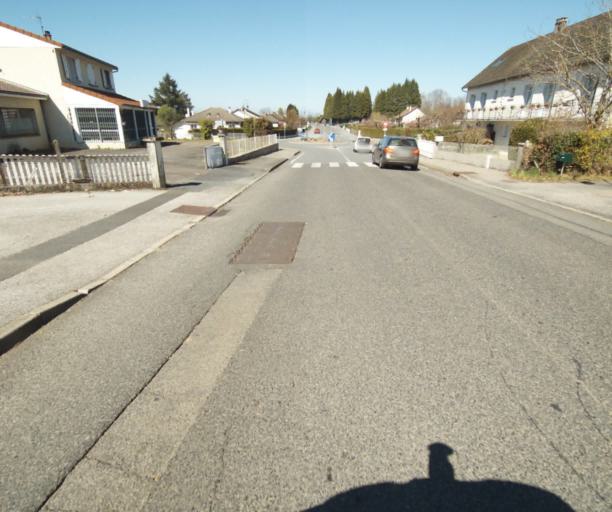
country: FR
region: Limousin
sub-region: Departement de la Correze
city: Saint-Mexant
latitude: 45.2805
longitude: 1.6601
